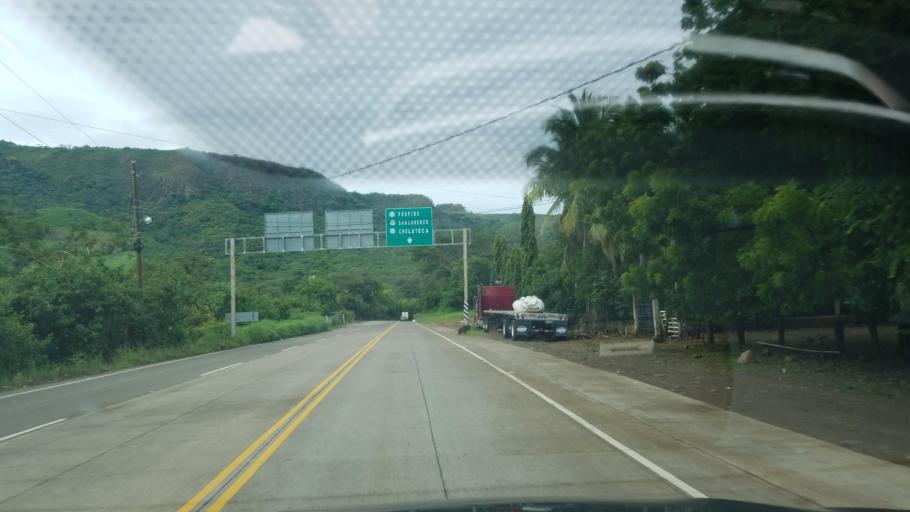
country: HN
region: Francisco Morazan
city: El Porvenir
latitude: 13.6922
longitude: -87.3293
